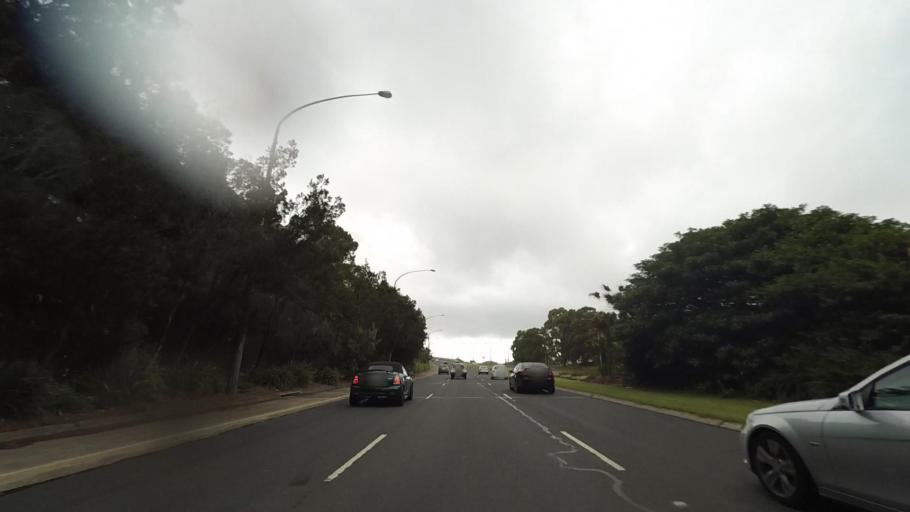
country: AU
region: New South Wales
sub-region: Kogarah
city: Blakehurst
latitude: -34.0126
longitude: 151.1252
